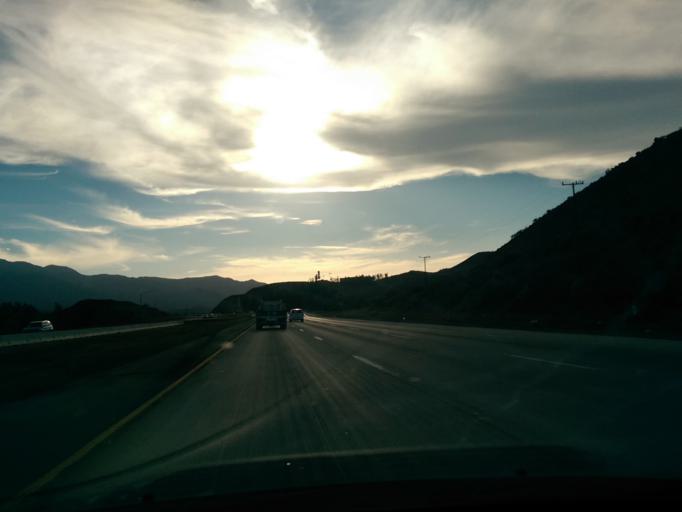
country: US
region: California
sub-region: Riverside County
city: Lake Elsinore
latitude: 33.7291
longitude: -117.3850
